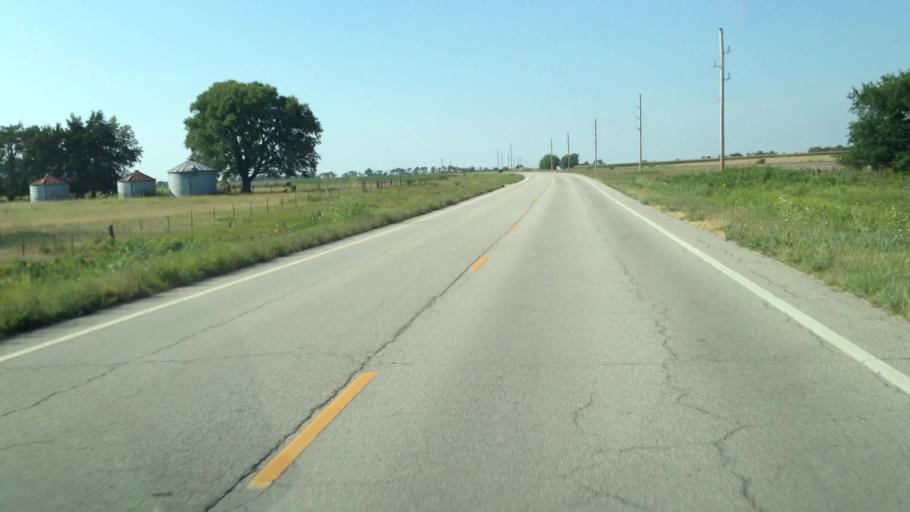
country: US
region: Kansas
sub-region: Allen County
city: Iola
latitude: 38.0042
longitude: -95.1704
